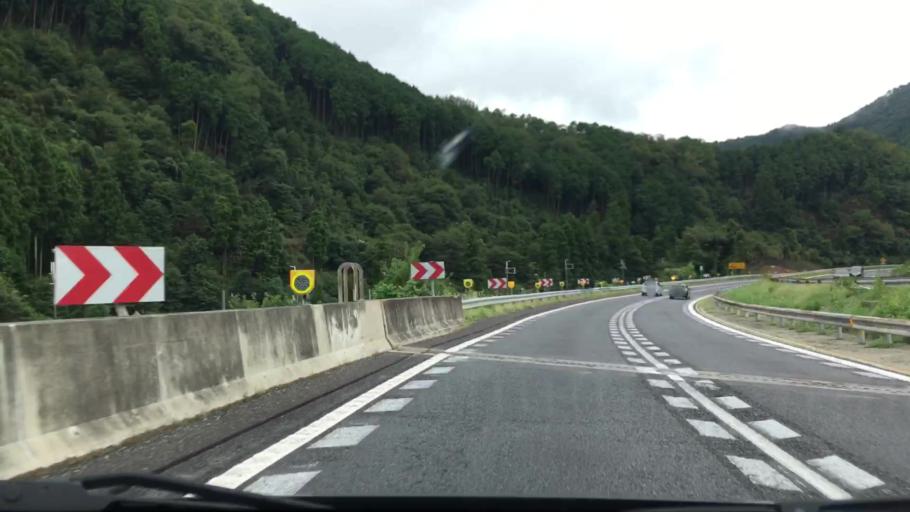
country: JP
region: Hyogo
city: Yamazakicho-nakabirose
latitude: 35.0423
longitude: 134.4486
